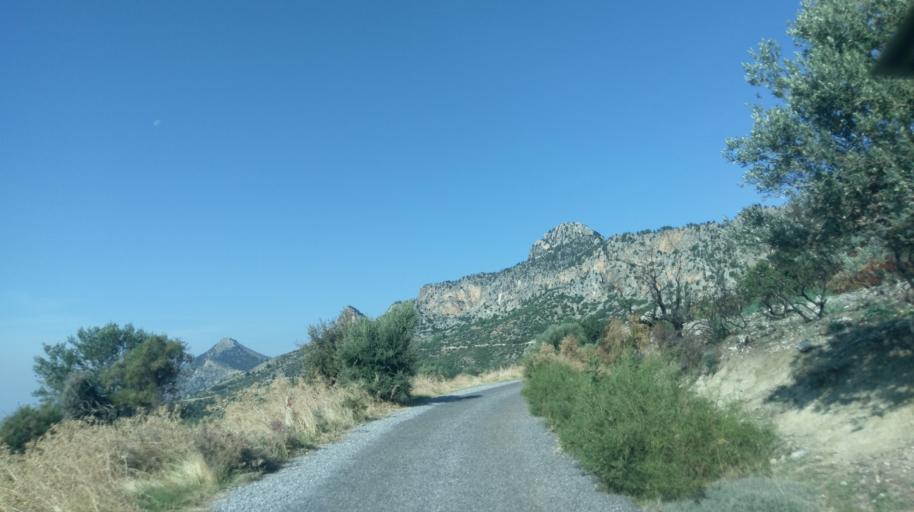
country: CY
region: Lefkosia
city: Nicosia
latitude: 35.2778
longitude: 33.4221
